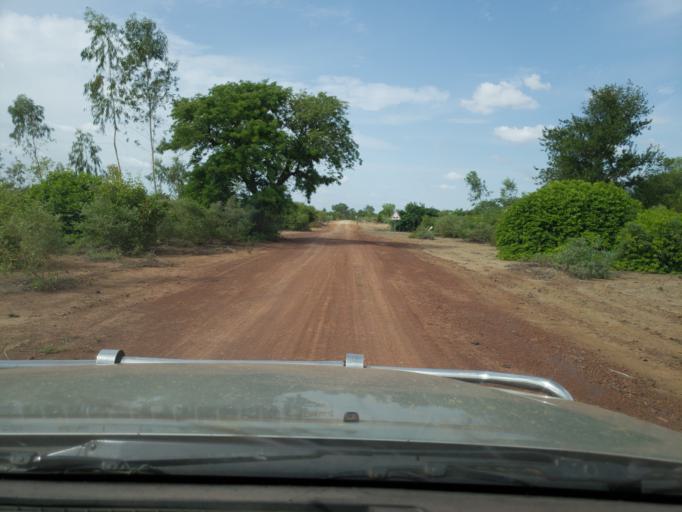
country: ML
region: Segou
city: Bla
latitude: 12.7629
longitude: -5.6232
